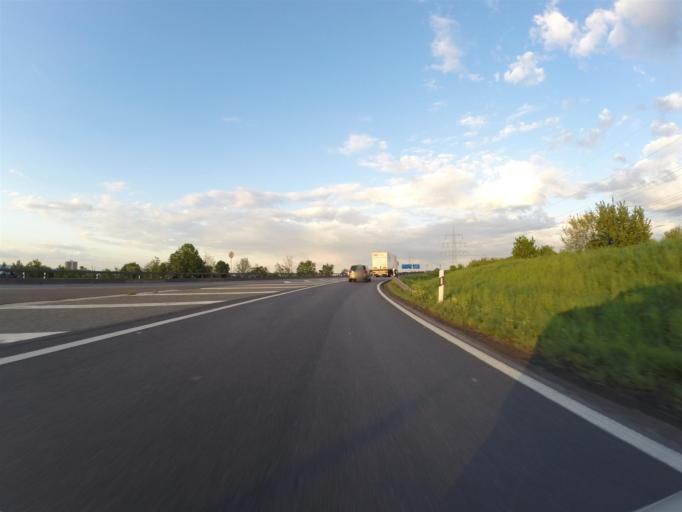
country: DE
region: Rheinland-Pfalz
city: Klein-Winternheim
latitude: 49.9643
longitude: 8.2421
